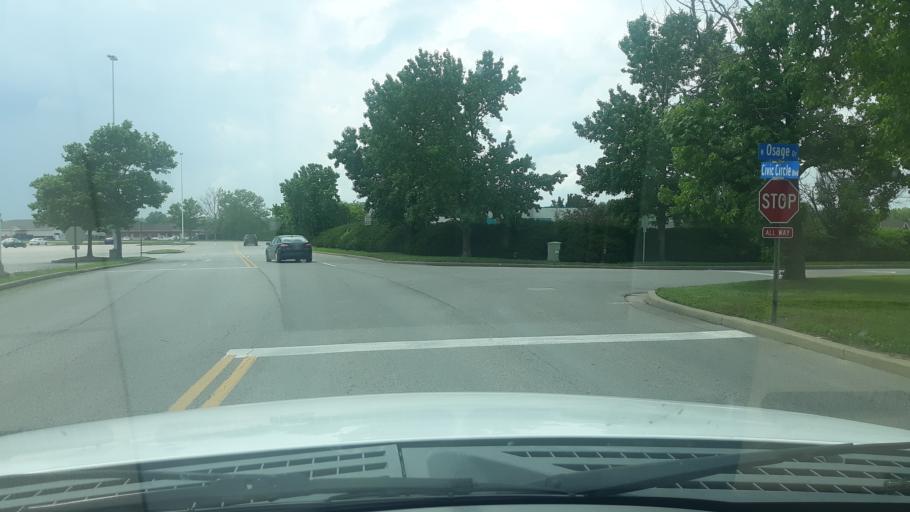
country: US
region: Illinois
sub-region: Williamson County
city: Marion
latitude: 37.7500
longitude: -88.9776
